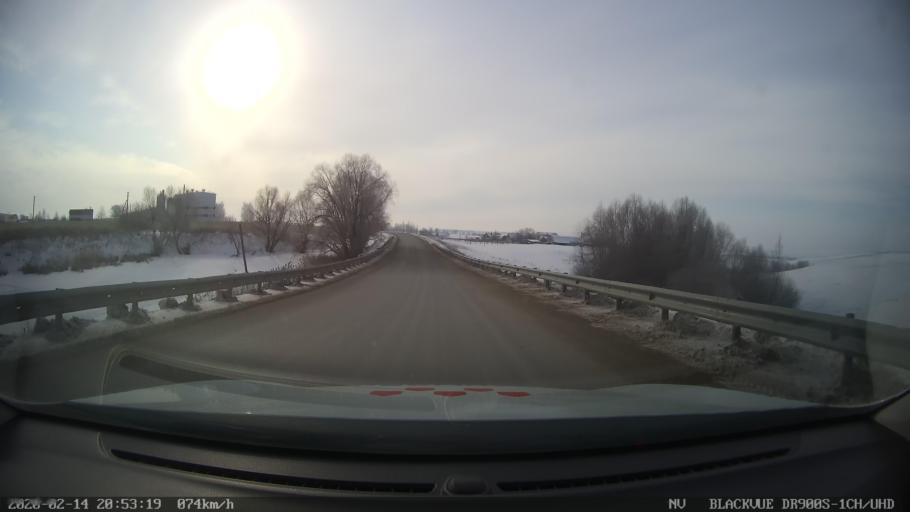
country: RU
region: Tatarstan
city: Kuybyshevskiy Zaton
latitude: 55.1959
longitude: 49.2474
